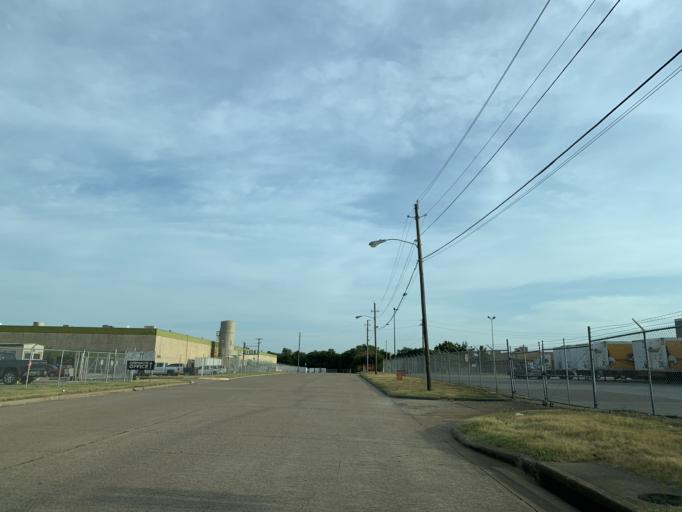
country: US
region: Texas
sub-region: Dallas County
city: Cockrell Hill
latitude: 32.7011
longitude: -96.9016
